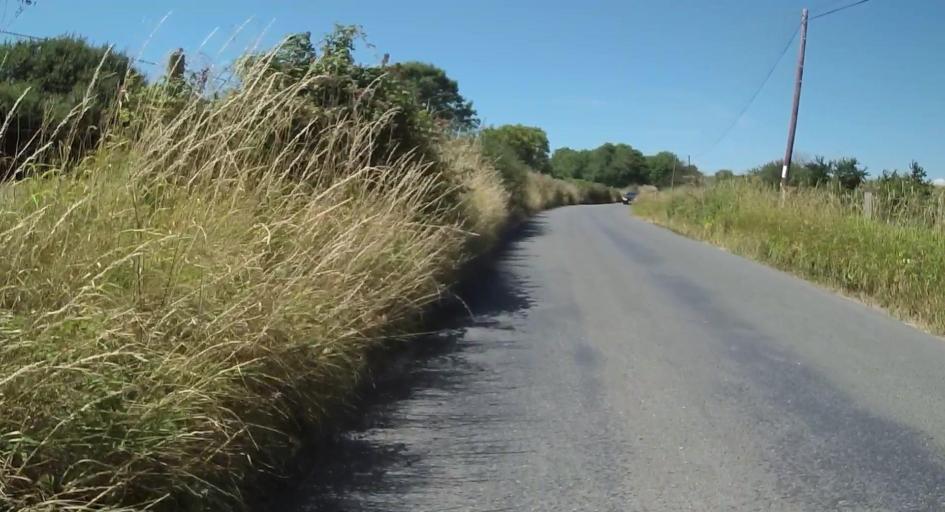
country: GB
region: England
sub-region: Dorset
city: Wareham
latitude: 50.6299
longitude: -2.1297
